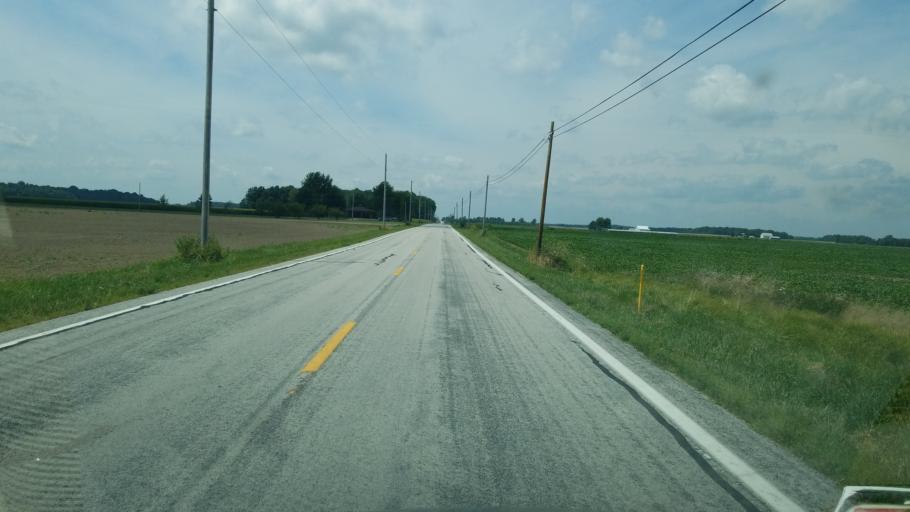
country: US
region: Ohio
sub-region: Hancock County
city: Arlington
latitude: 40.8914
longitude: -83.5774
